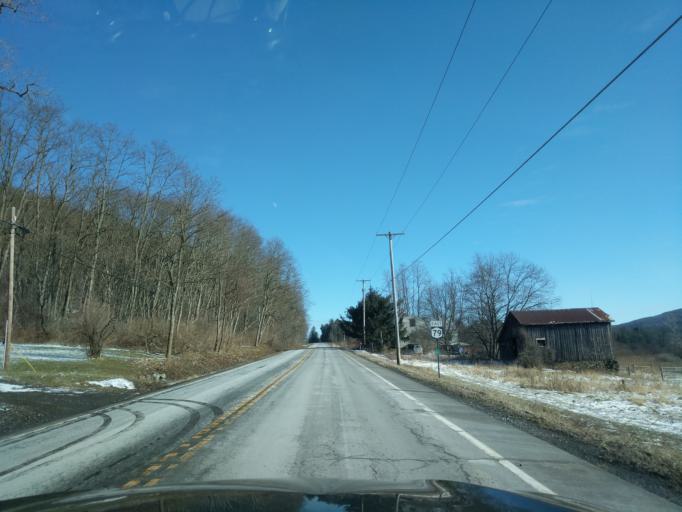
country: US
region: New York
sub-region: Tompkins County
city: East Ithaca
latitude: 42.3955
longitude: -76.3979
